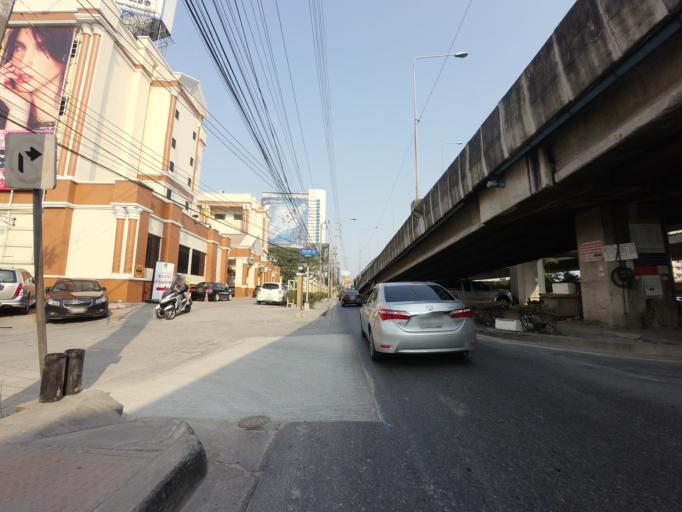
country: TH
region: Bangkok
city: Huai Khwang
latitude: 13.7548
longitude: 100.5839
